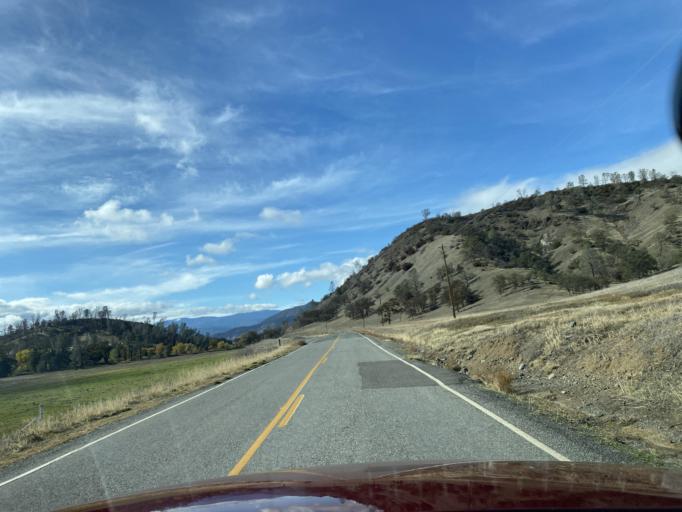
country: US
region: California
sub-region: Glenn County
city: Willows
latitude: 39.4250
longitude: -122.5292
